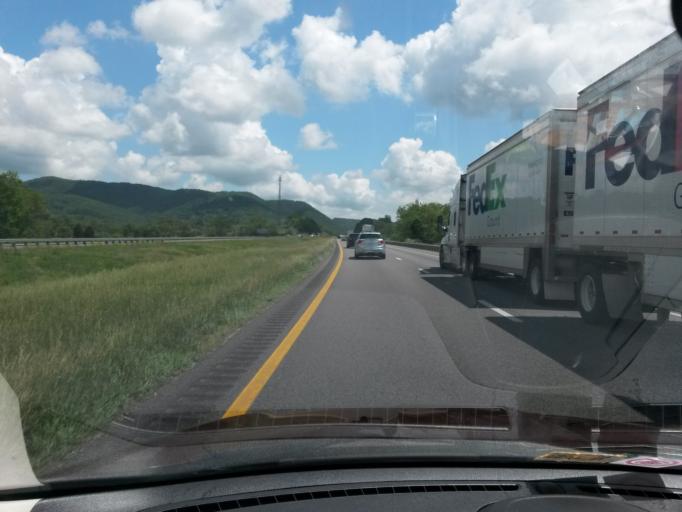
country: US
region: Virginia
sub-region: Carroll County
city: Woodlawn
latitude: 36.8631
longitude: -80.8704
